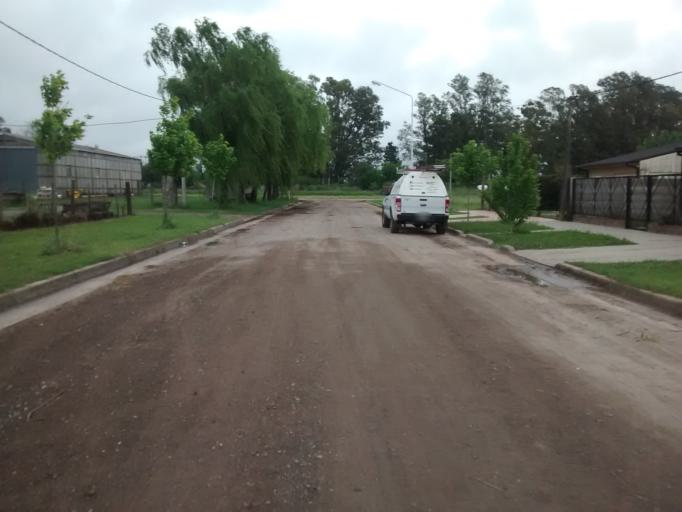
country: AR
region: Santa Fe
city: Galvez
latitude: -31.9014
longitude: -61.2805
